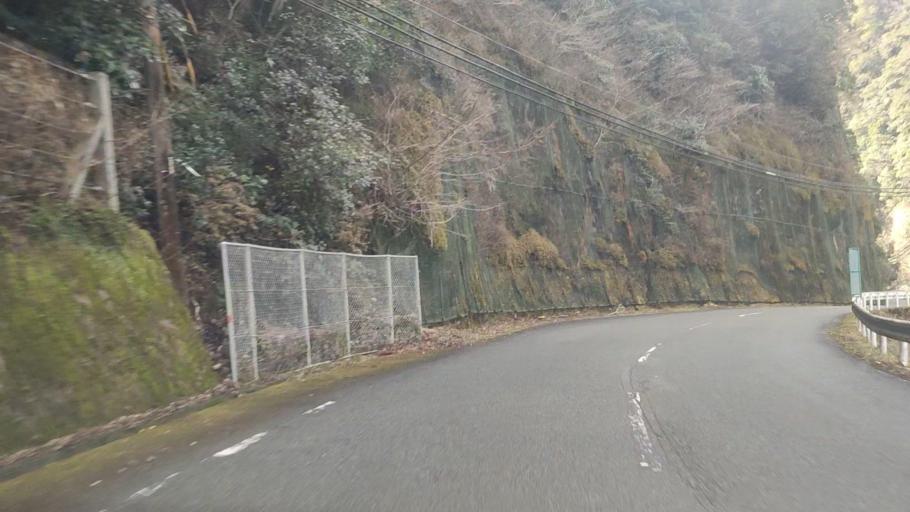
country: JP
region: Kumamoto
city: Hitoyoshi
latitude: 32.4245
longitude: 130.8566
